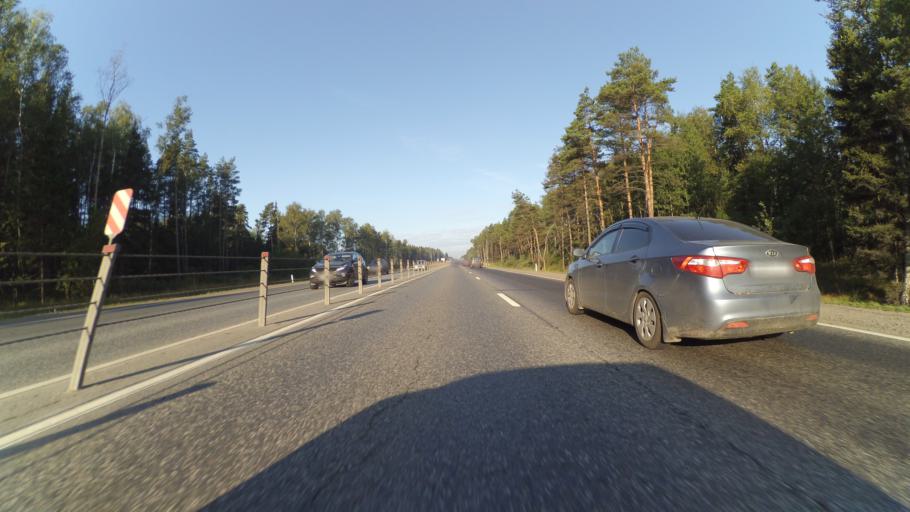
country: RU
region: Moskovskaya
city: Chupryakovo
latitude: 55.5633
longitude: 36.6221
